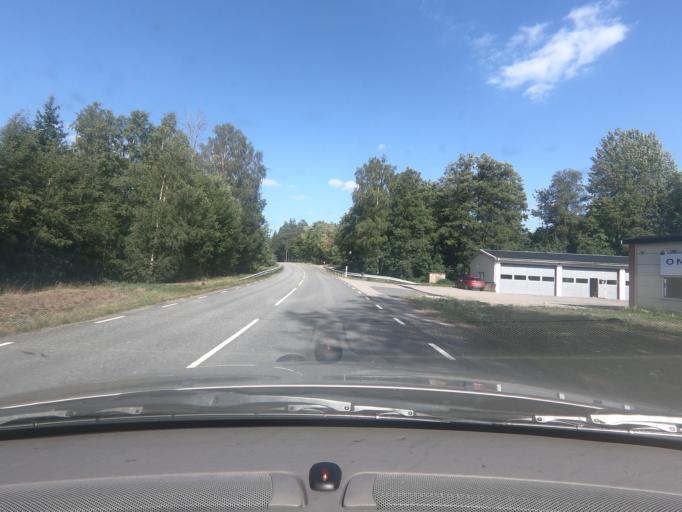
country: SE
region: Joenkoeping
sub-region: Vetlanda Kommun
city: Landsbro
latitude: 57.3723
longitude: 14.9267
